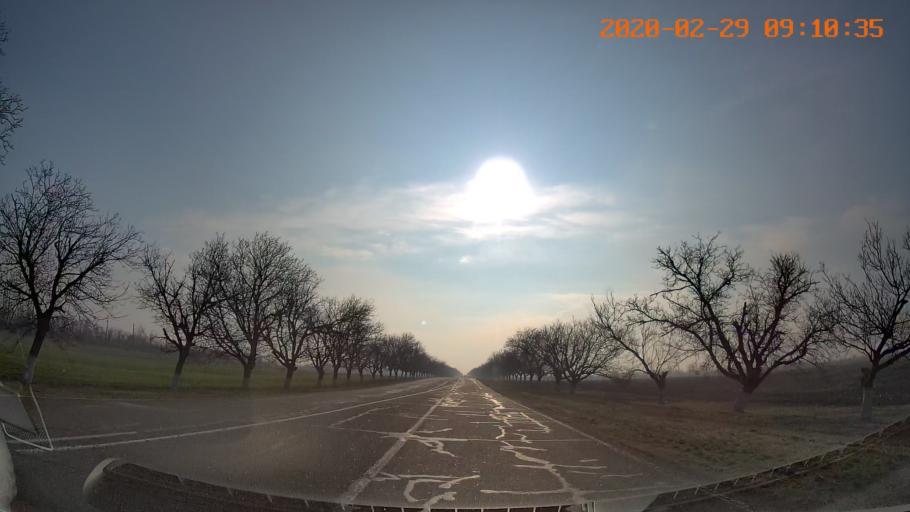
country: MD
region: Telenesti
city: Slobozia
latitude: 46.8428
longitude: 29.7846
